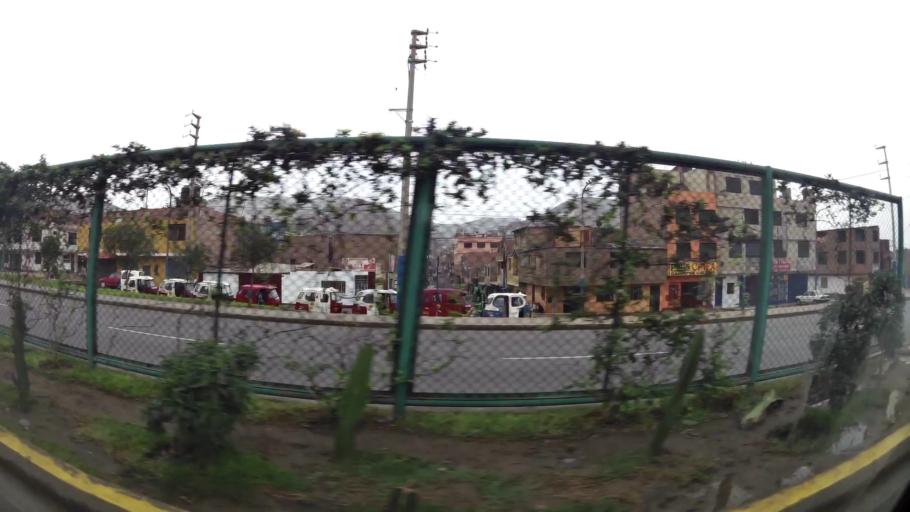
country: PE
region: Lima
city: Ventanilla
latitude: -11.8983
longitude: -77.1272
